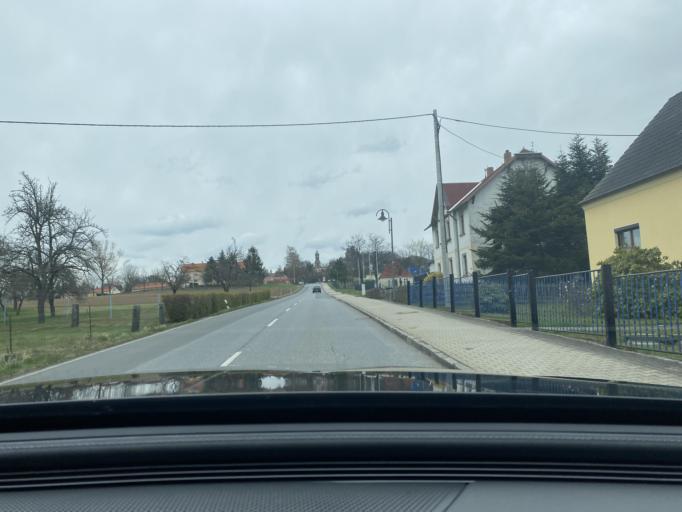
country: DE
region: Saxony
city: Stolpen
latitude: 51.0446
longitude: 14.0705
